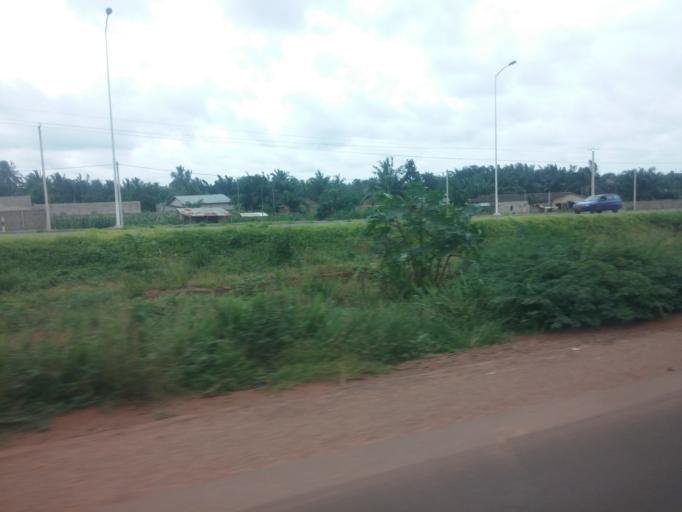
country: TG
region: Maritime
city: Tsevie
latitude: 6.3171
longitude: 1.2172
